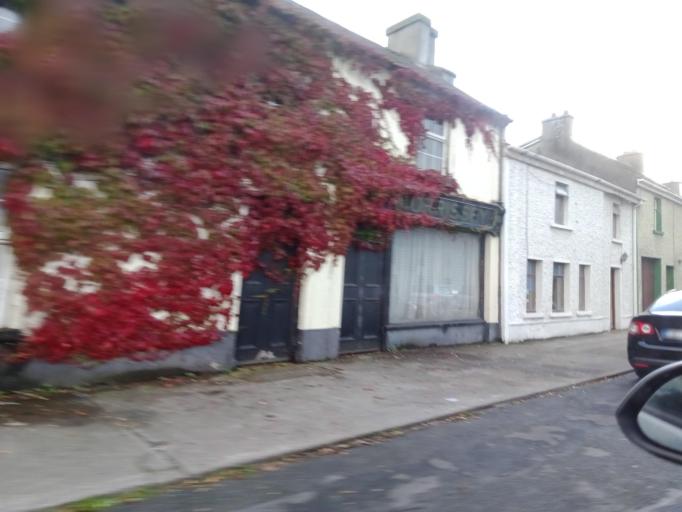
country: IE
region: Leinster
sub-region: Uibh Fhaili
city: Tullamore
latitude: 53.1482
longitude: -7.5228
